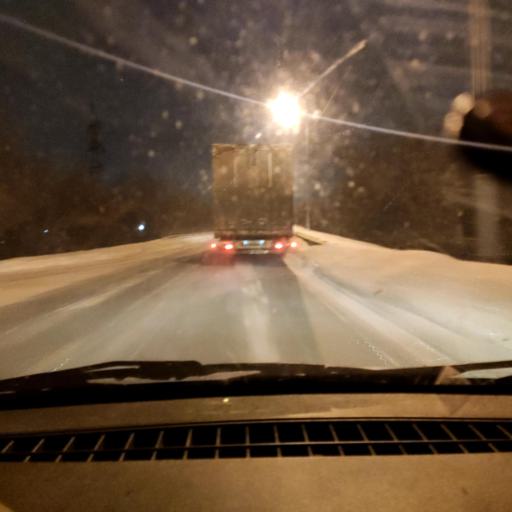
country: RU
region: Bashkortostan
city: Blagoveshchensk
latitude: 54.9207
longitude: 56.0821
